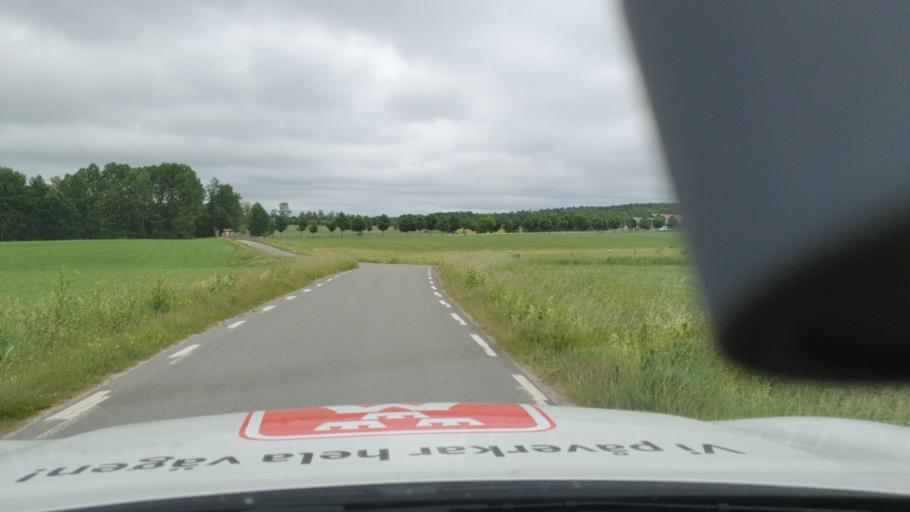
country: SE
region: Vaestra Goetaland
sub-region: Tibro Kommun
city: Tibro
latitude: 58.3678
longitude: 14.1704
